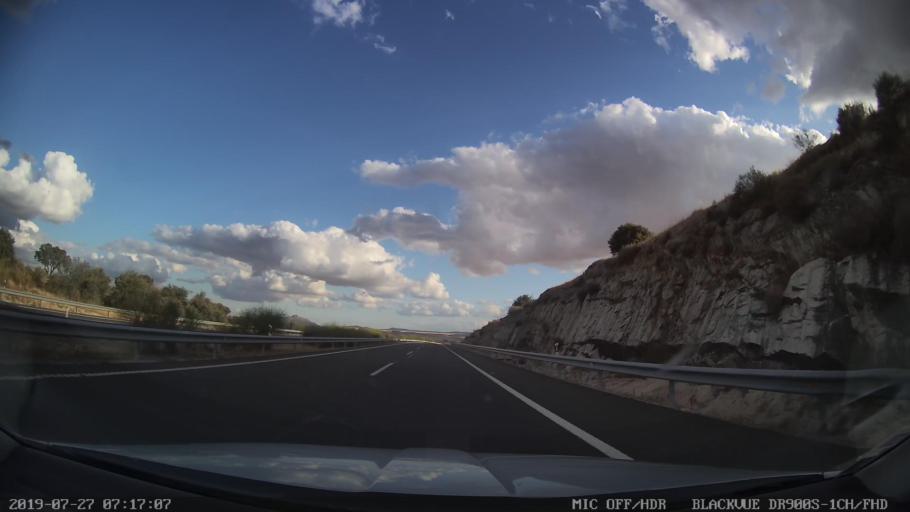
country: ES
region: Extremadura
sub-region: Provincia de Caceres
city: Trujillo
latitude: 39.4452
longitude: -5.8746
